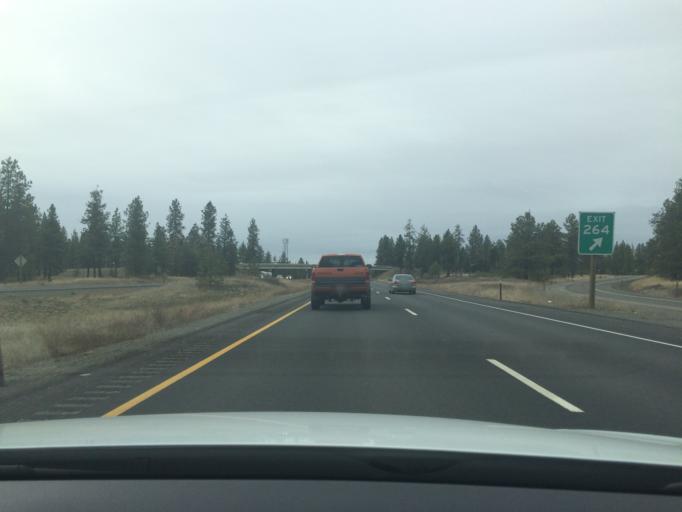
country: US
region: Washington
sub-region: Spokane County
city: Medical Lake
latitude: 47.5062
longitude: -117.6885
